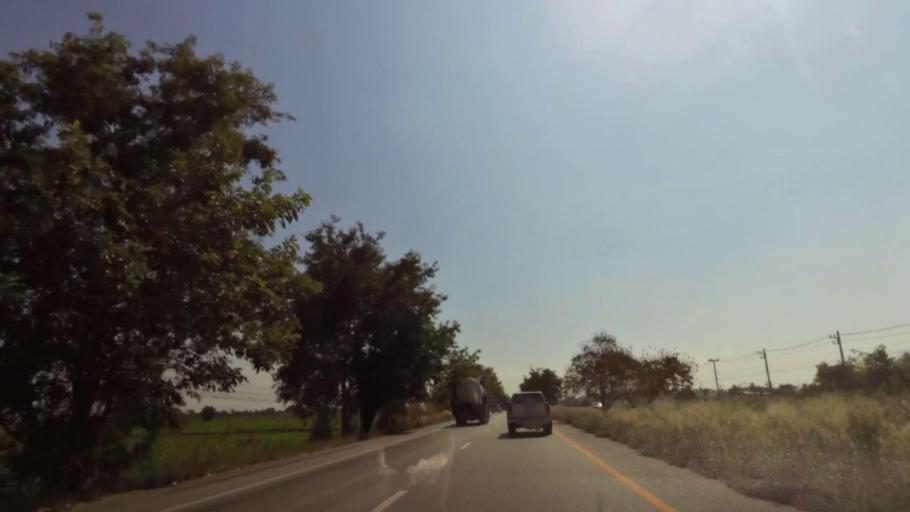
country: TH
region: Nakhon Sawan
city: Kao Liao
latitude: 15.8349
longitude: 100.1179
